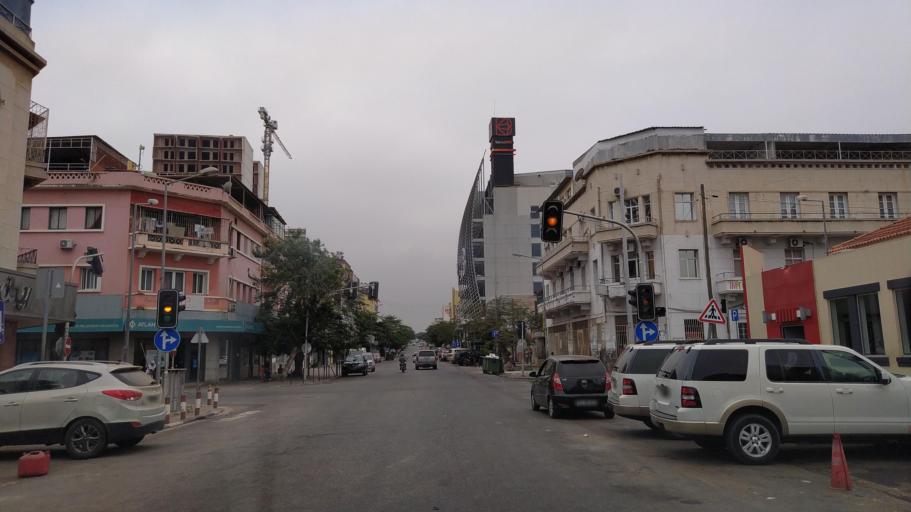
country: AO
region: Luanda
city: Luanda
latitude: -8.8191
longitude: 13.2386
